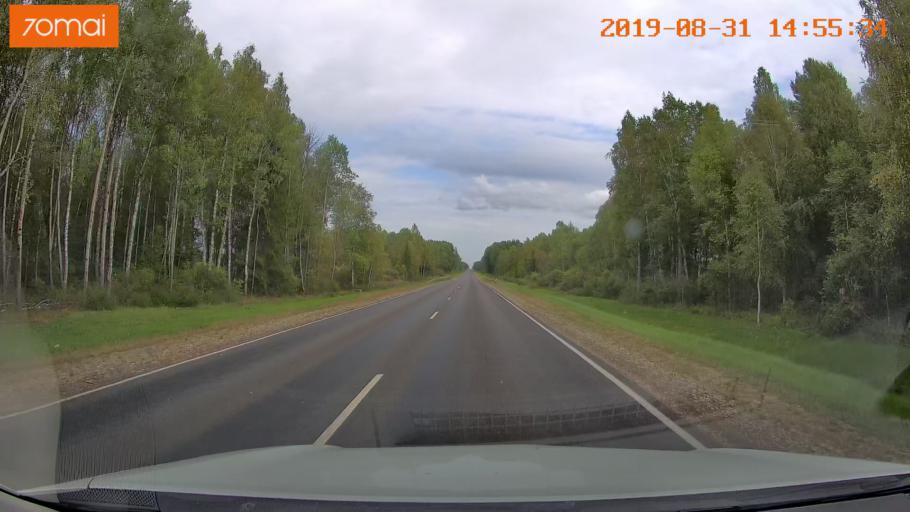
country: RU
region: Kaluga
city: Spas-Demensk
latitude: 54.2988
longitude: 33.9173
